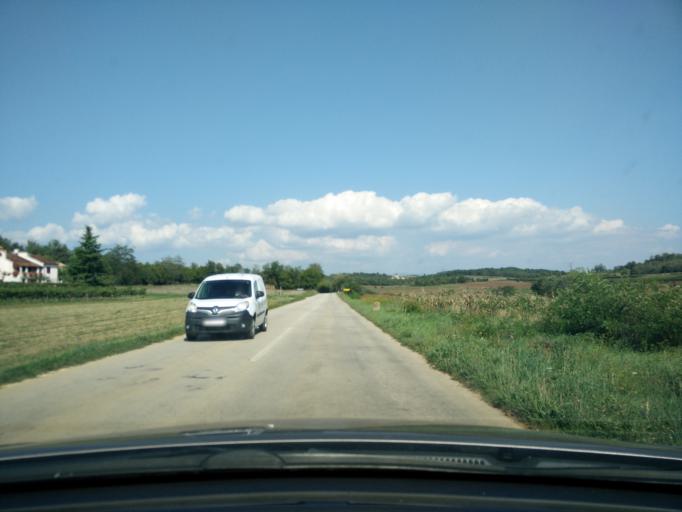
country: HR
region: Istarska
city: Karojba
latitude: 45.3214
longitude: 13.7356
